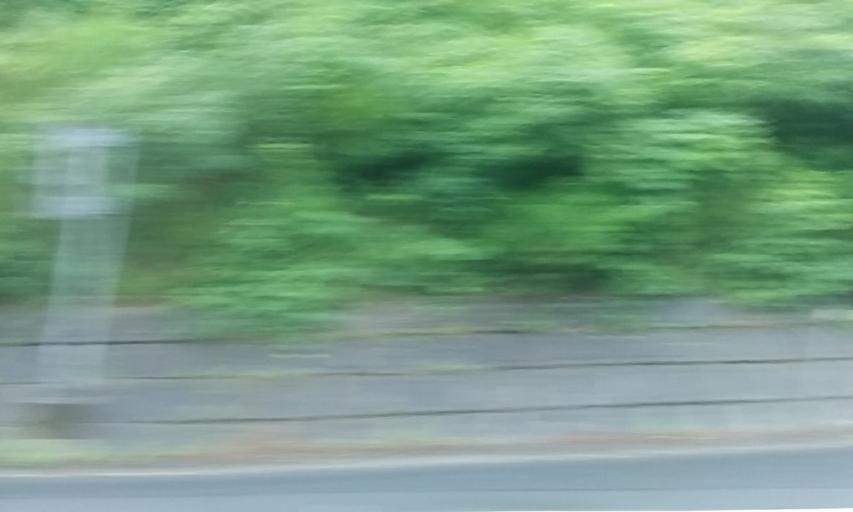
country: JP
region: Fukushima
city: Motomiya
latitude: 37.4849
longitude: 140.3253
